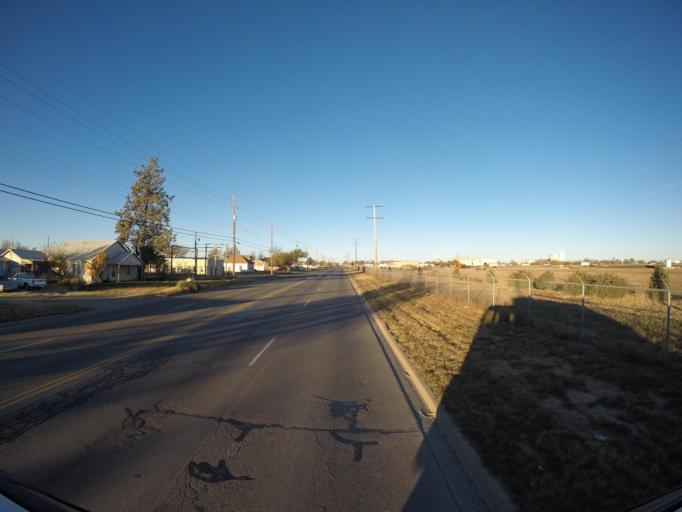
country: US
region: New Mexico
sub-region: Curry County
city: Clovis
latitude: 34.3902
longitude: -103.1881
